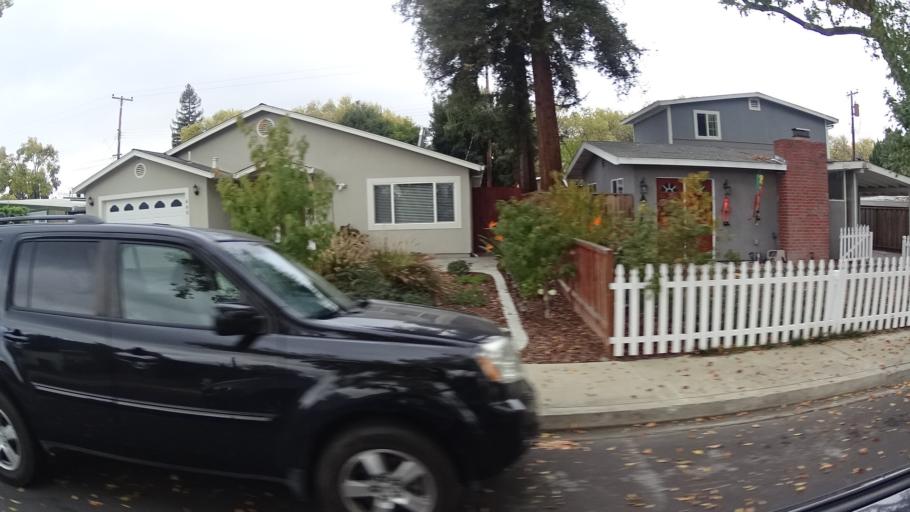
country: US
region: California
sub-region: Santa Clara County
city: Santa Clara
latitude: 37.3342
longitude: -121.9811
